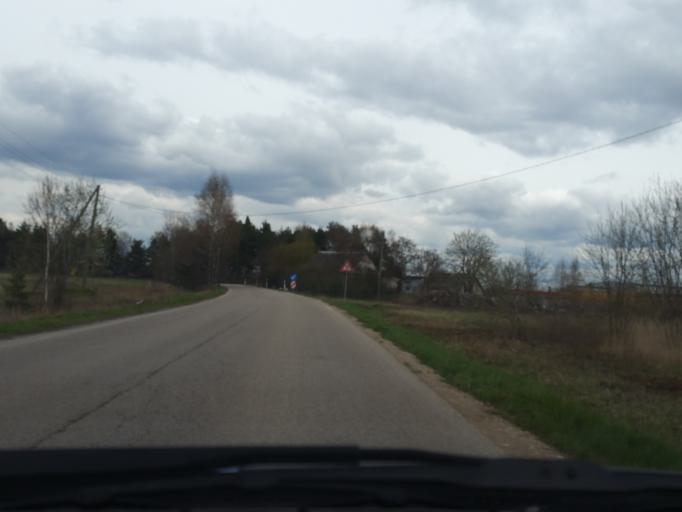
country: LV
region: Marupe
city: Marupe
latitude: 56.9207
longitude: 24.0011
